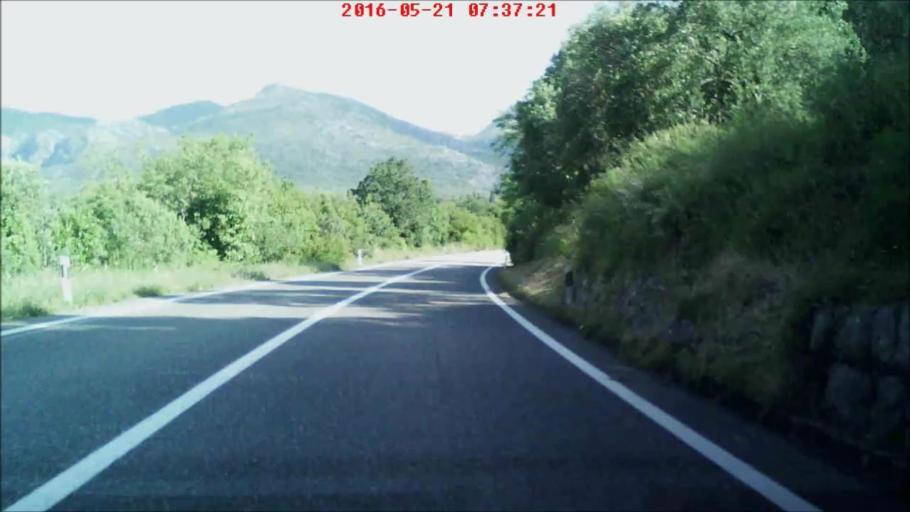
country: HR
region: Dubrovacko-Neretvanska
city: Podgora
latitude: 42.7896
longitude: 17.8544
